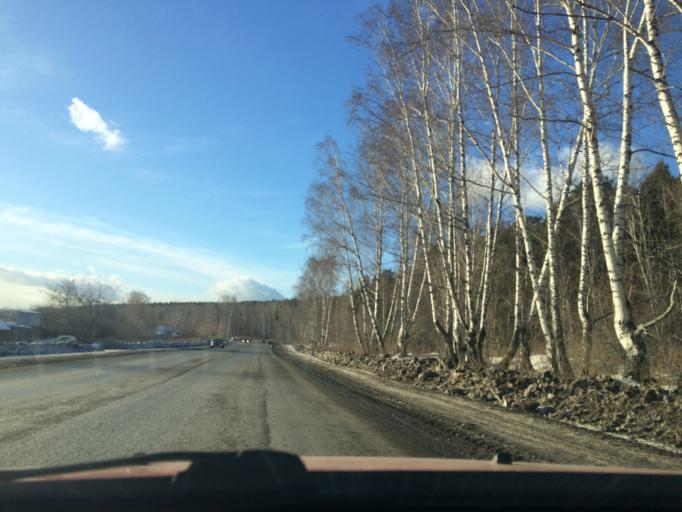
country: RU
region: Sverdlovsk
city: Istok
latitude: 56.7865
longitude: 60.7619
